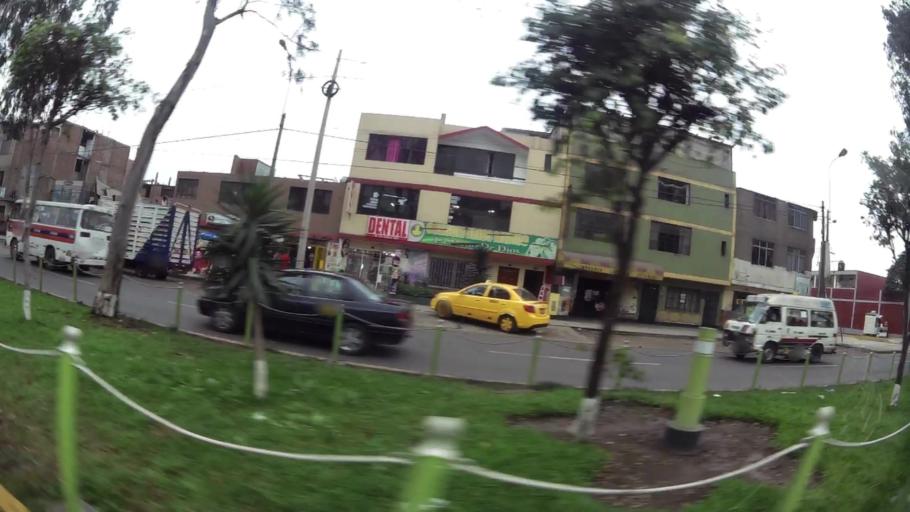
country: PE
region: Lima
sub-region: Lima
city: Vitarte
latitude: -12.0392
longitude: -76.9681
